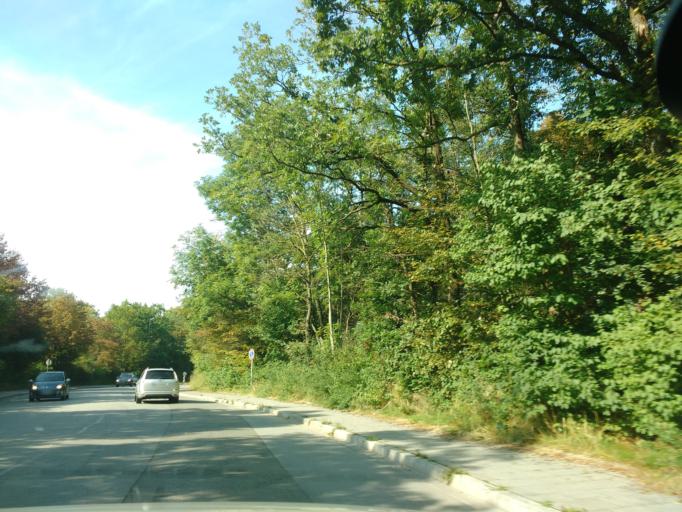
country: DE
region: Bavaria
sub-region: Upper Bavaria
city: Grafelfing
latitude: 48.1188
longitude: 11.4506
